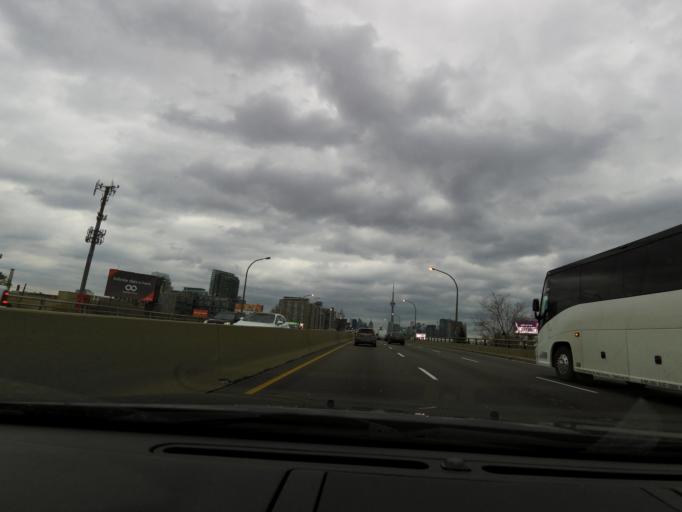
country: CA
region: Ontario
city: Toronto
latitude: 43.6347
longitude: -79.4219
